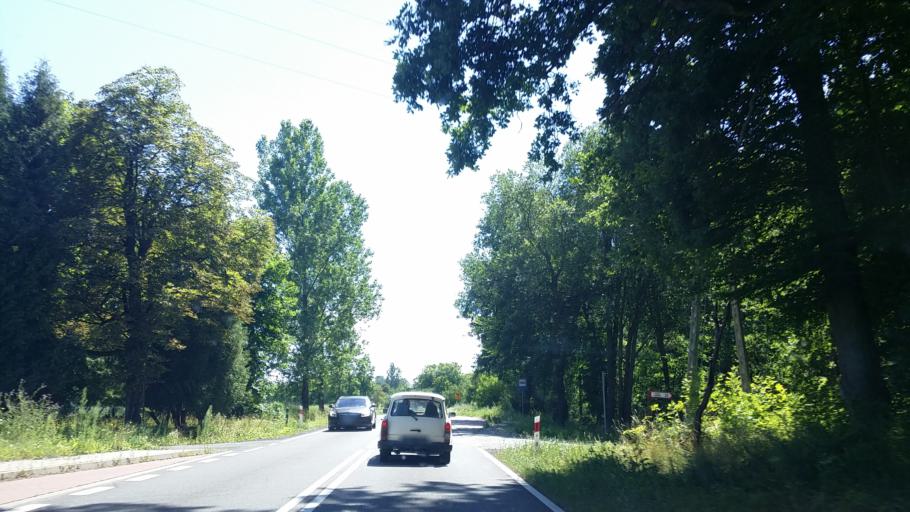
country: PL
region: West Pomeranian Voivodeship
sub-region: Powiat stargardzki
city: Insko
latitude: 53.4732
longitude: 15.5780
